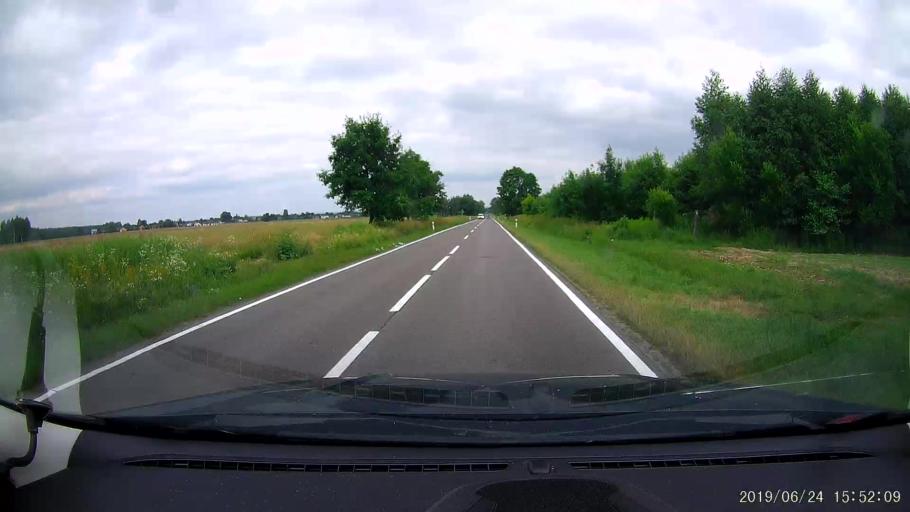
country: PL
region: Subcarpathian Voivodeship
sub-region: Powiat lubaczowski
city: Lubaczow
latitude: 50.1986
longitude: 23.0866
